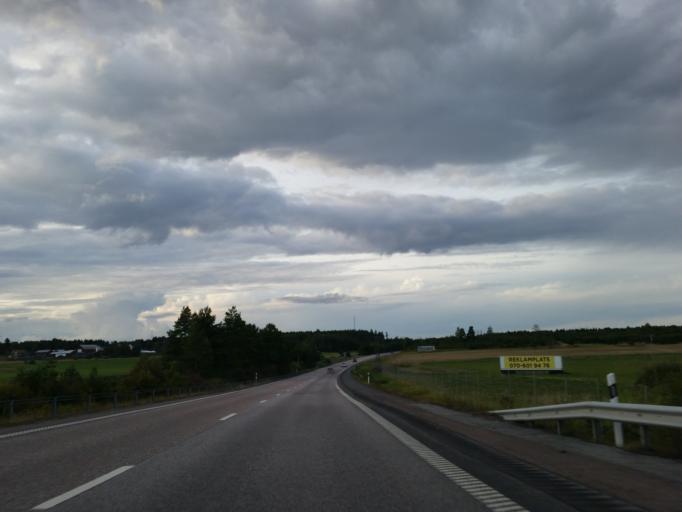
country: SE
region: Stockholm
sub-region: Sigtuna Kommun
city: Marsta
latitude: 59.6743
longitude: 17.8716
